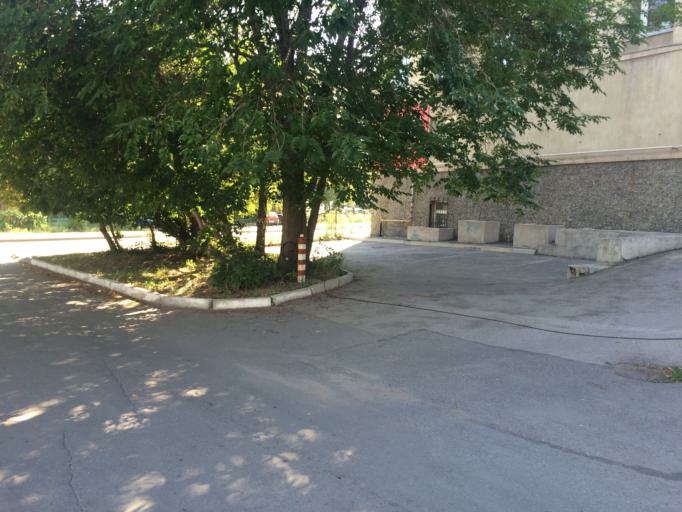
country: RU
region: Chelyabinsk
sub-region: Gorod Magnitogorsk
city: Magnitogorsk
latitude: 53.3963
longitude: 58.9738
